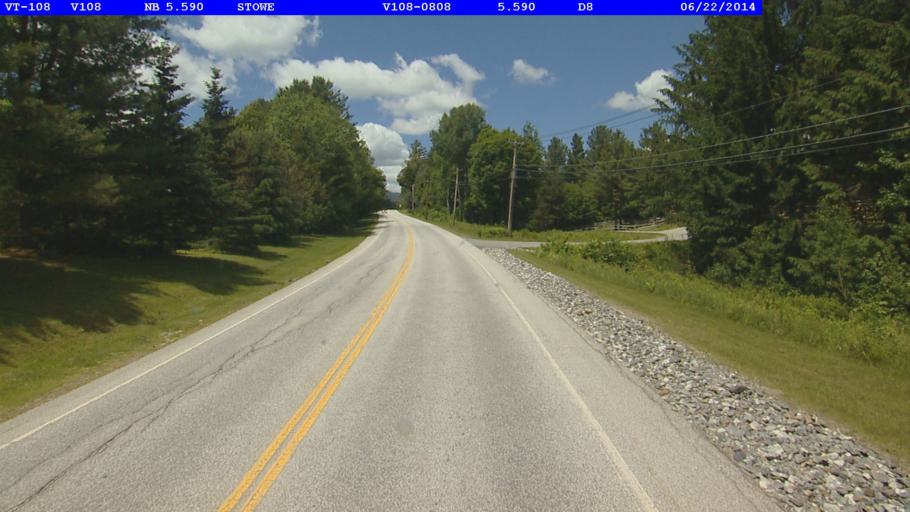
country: US
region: Vermont
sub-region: Lamoille County
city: Morristown
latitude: 44.5068
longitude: -72.7620
